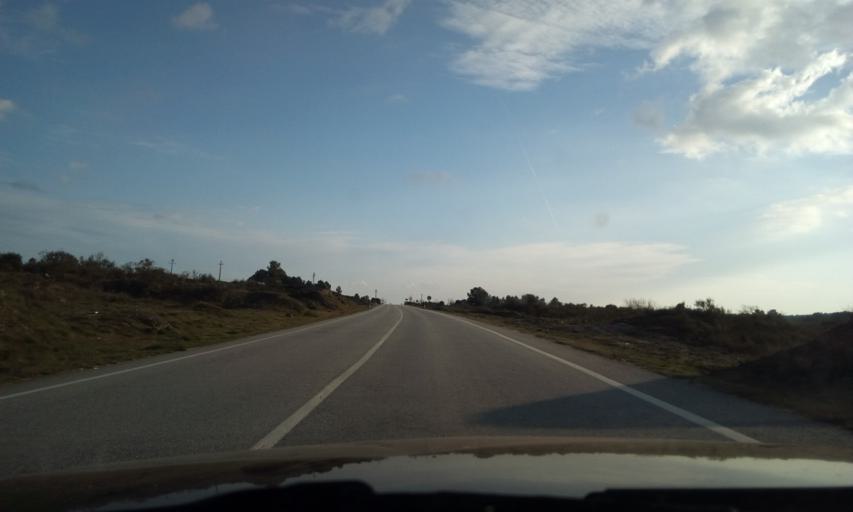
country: ES
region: Castille and Leon
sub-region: Provincia de Salamanca
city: Fuentes de Onoro
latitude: 40.6353
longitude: -6.9729
